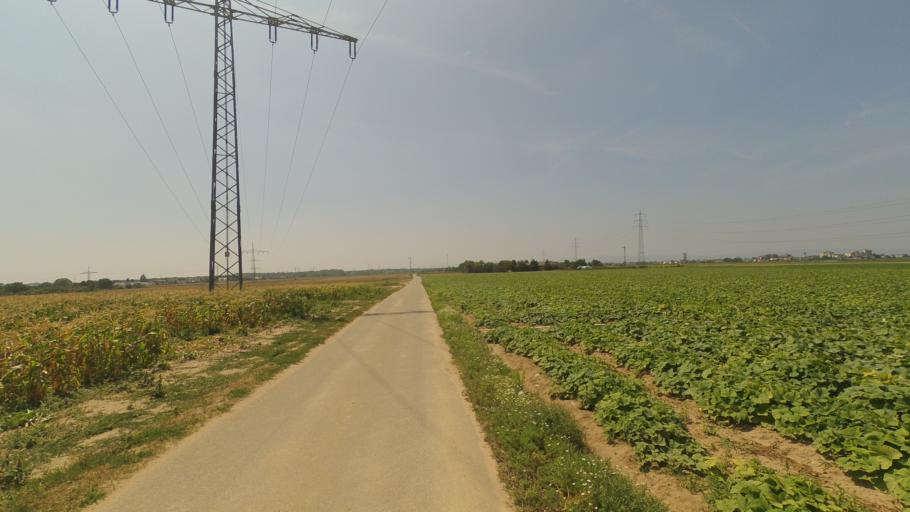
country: DE
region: Rheinland-Pfalz
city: Limburgerhof
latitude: 49.4342
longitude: 8.3884
